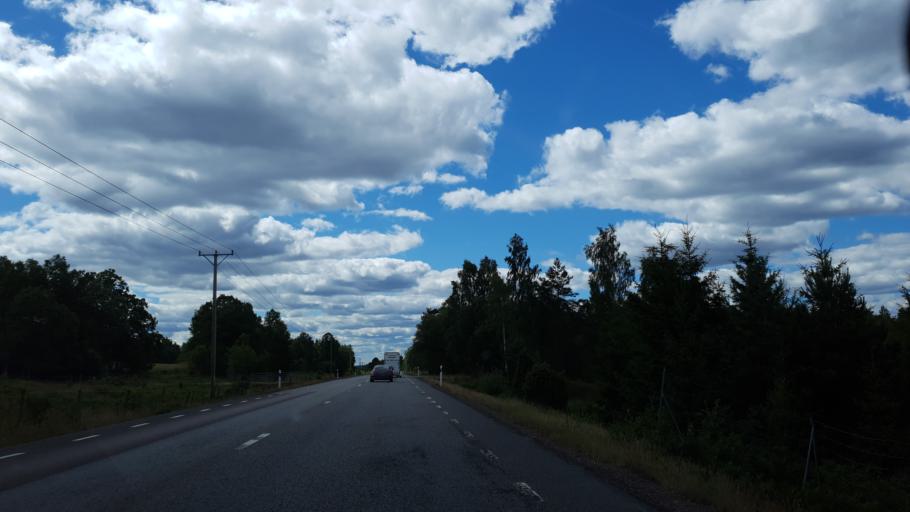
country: SE
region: Kronoberg
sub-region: Vaxjo Kommun
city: Braas
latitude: 57.1620
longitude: 15.1619
